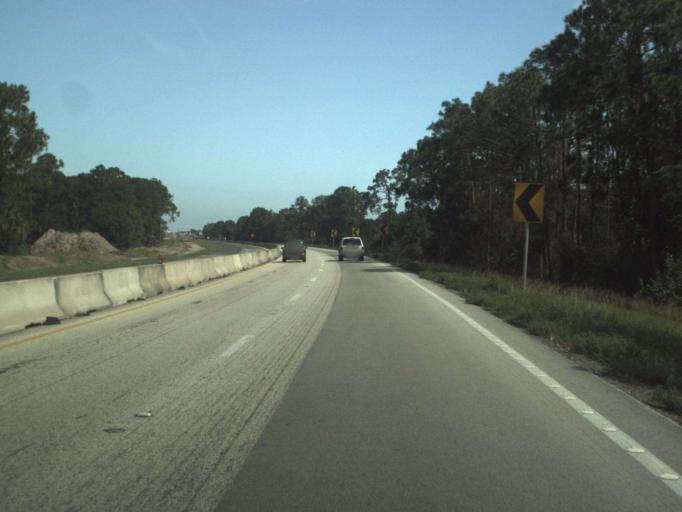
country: US
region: Florida
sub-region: Indian River County
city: Roseland
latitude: 27.8158
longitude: -80.5489
